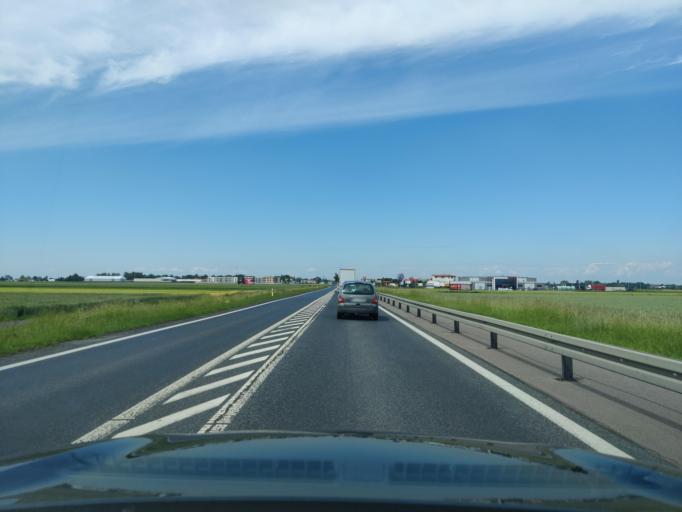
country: PL
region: Greater Poland Voivodeship
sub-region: Powiat grodziski
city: Granowo
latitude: 52.2219
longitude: 16.5502
